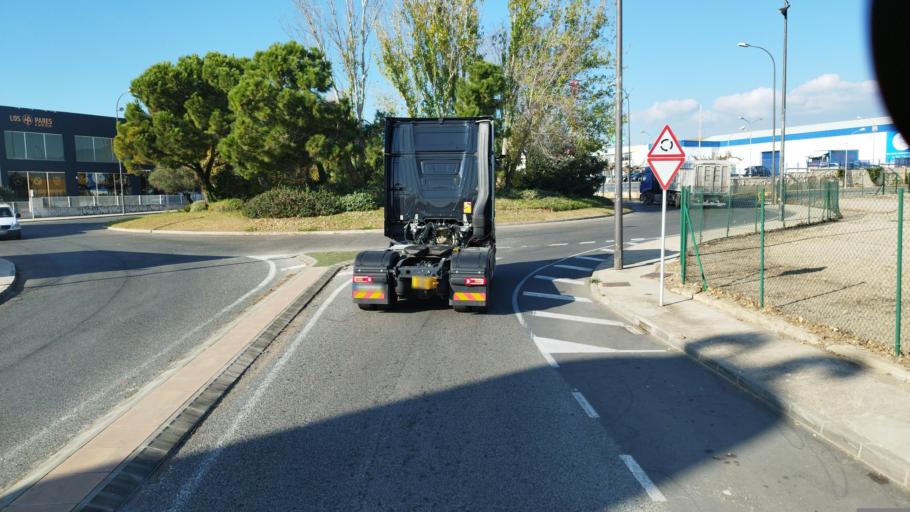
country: ES
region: Catalonia
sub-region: Provincia de Tarragona
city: Reus
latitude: 41.1607
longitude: 1.0823
